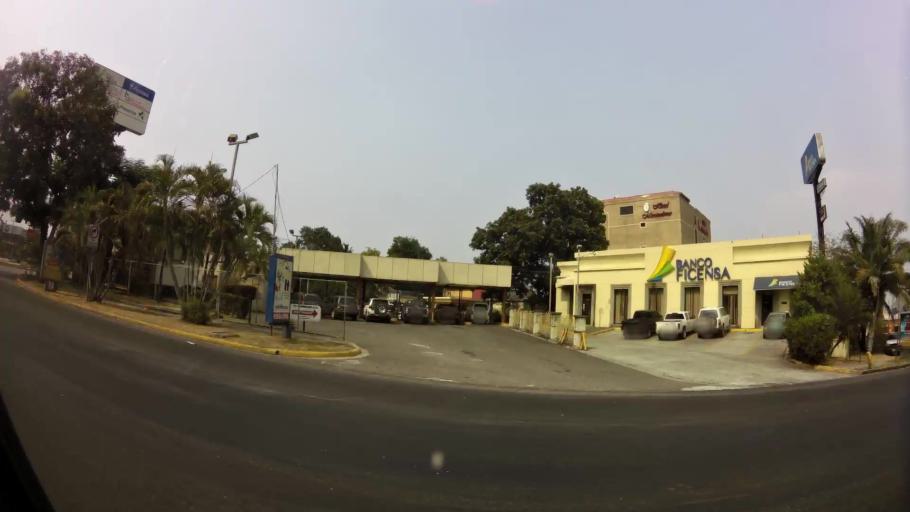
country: HN
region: Cortes
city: Armenta
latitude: 15.4987
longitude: -88.0370
